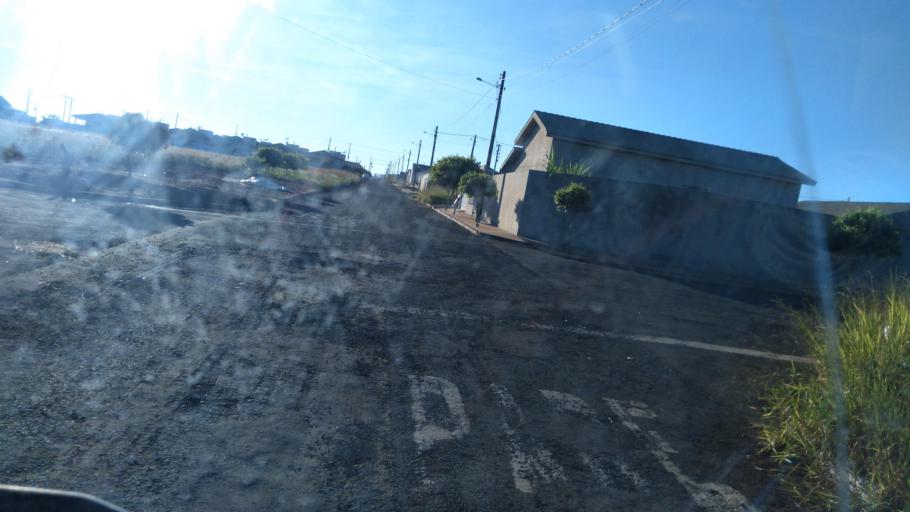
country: BR
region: Goias
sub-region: Mineiros
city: Mineiros
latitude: -17.5444
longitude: -52.5565
